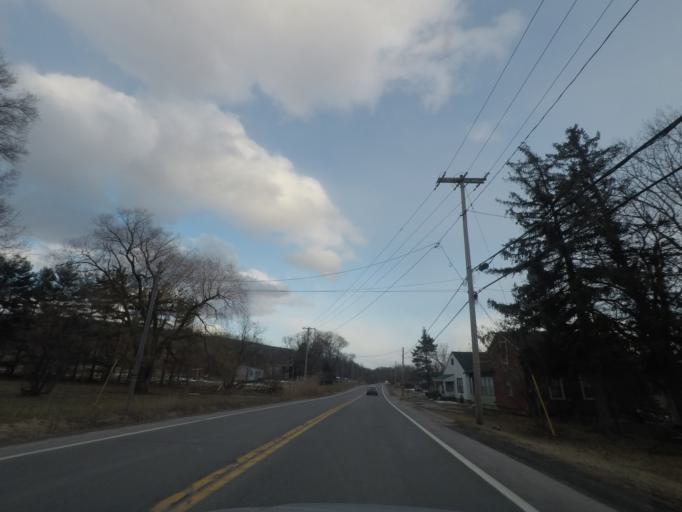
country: US
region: New York
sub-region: Herkimer County
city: Frankfort
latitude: 43.0492
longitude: -75.0669
